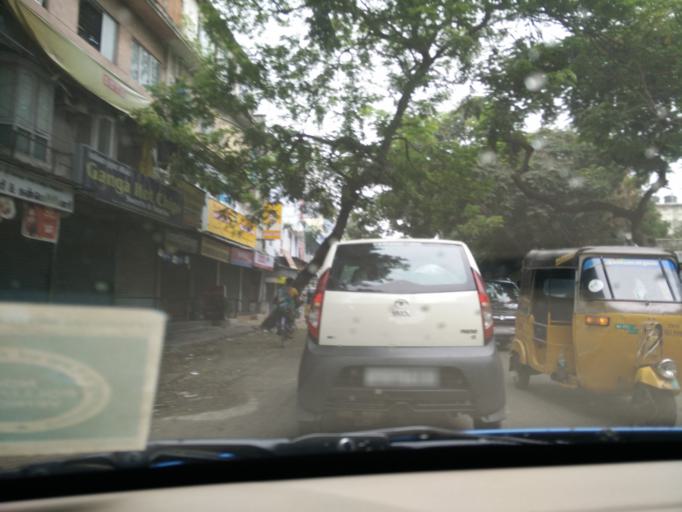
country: IN
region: Tamil Nadu
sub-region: Chennai
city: Gandhi Nagar
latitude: 13.0031
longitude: 80.2519
